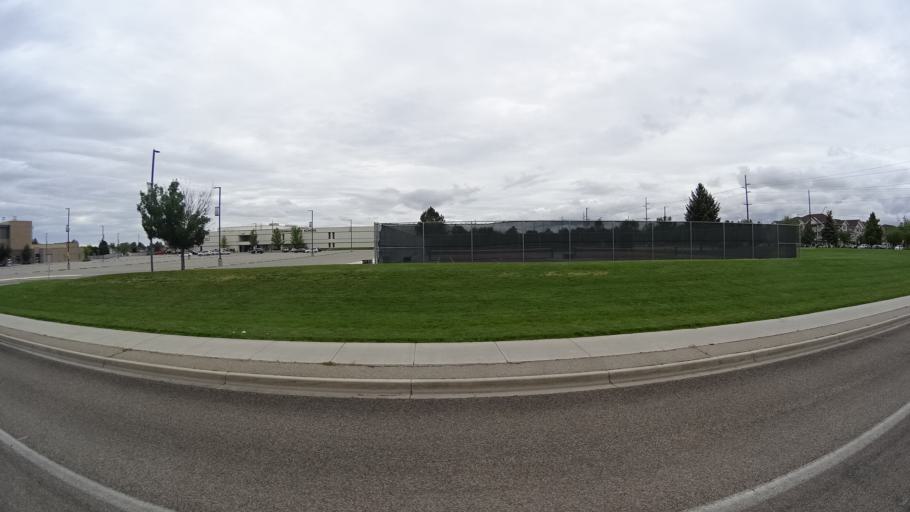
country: US
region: Idaho
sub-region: Ada County
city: Eagle
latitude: 43.6485
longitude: -116.3353
